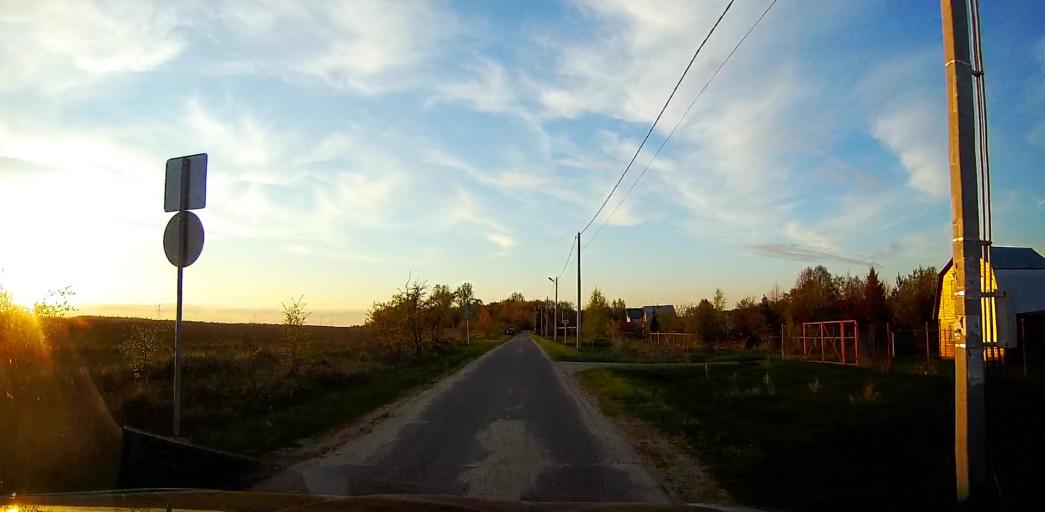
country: RU
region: Moskovskaya
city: Peski
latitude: 55.2294
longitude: 38.7335
